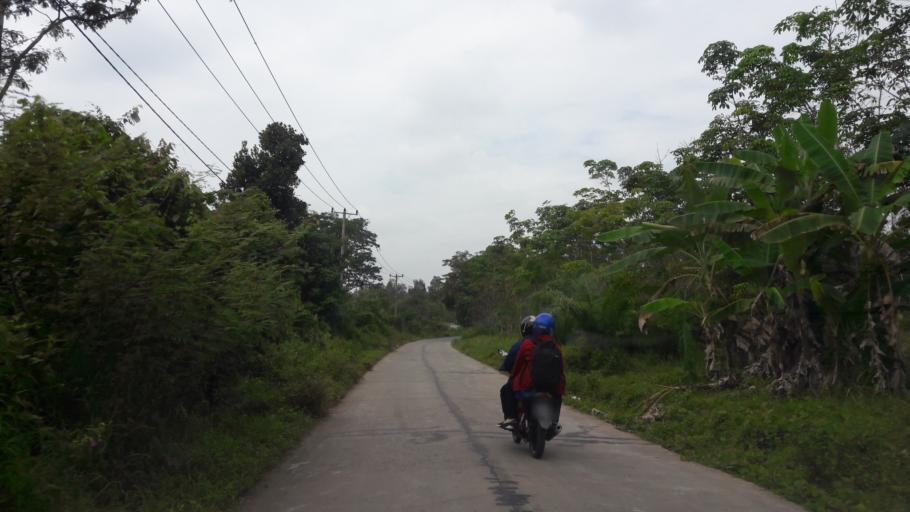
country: ID
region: South Sumatra
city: Gunungmenang
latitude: -3.2274
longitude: 104.1107
